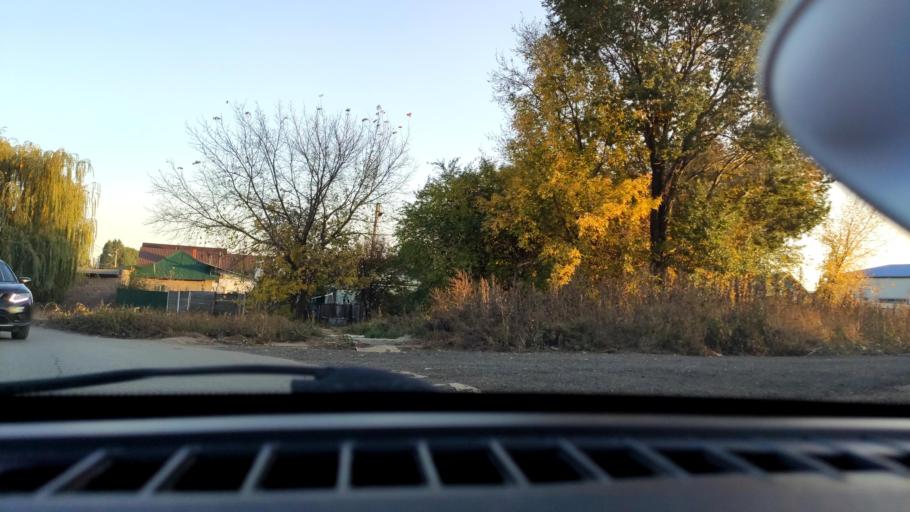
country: RU
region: Samara
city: Samara
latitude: 53.2343
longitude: 50.2327
